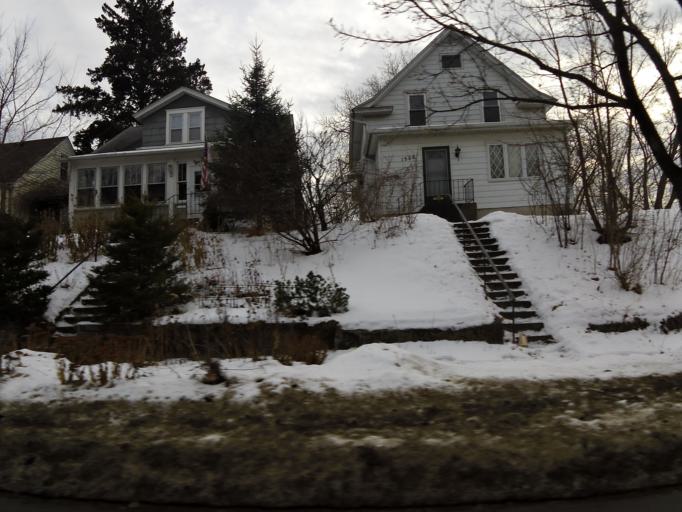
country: US
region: Minnesota
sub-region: Ramsey County
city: Maplewood
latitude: 44.9667
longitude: -93.0344
